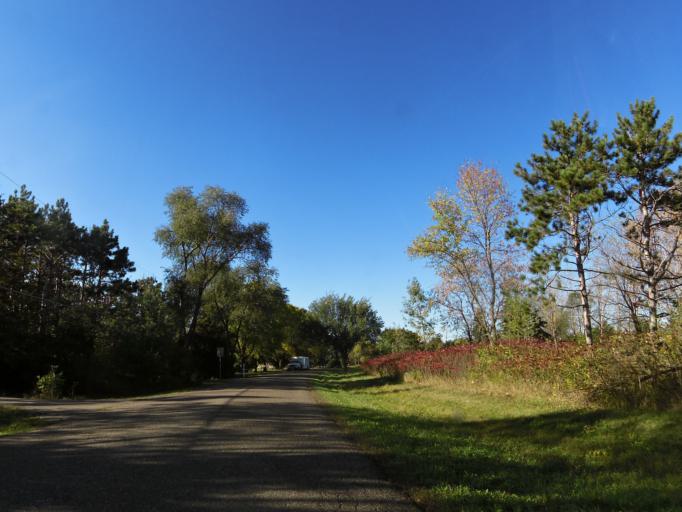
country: US
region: Minnesota
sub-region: Washington County
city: Lakeland
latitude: 44.9532
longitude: -92.7435
